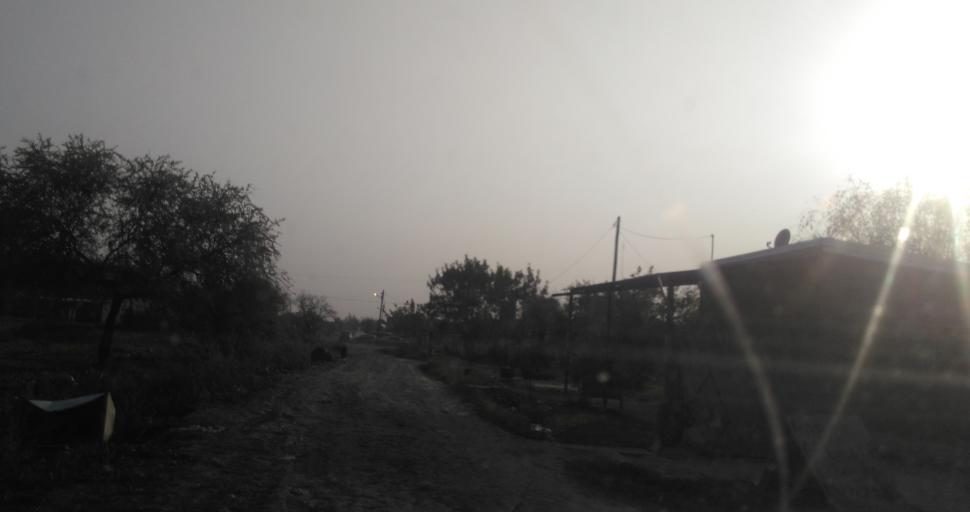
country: AR
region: Chaco
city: Resistencia
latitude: -27.4720
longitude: -59.0184
